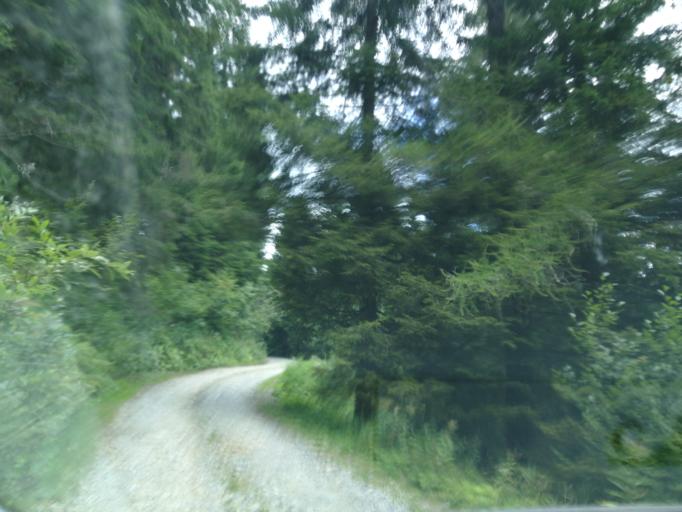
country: IT
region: Trentino-Alto Adige
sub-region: Provincia di Trento
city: Castel Condino
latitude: 45.9385
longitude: 10.5597
